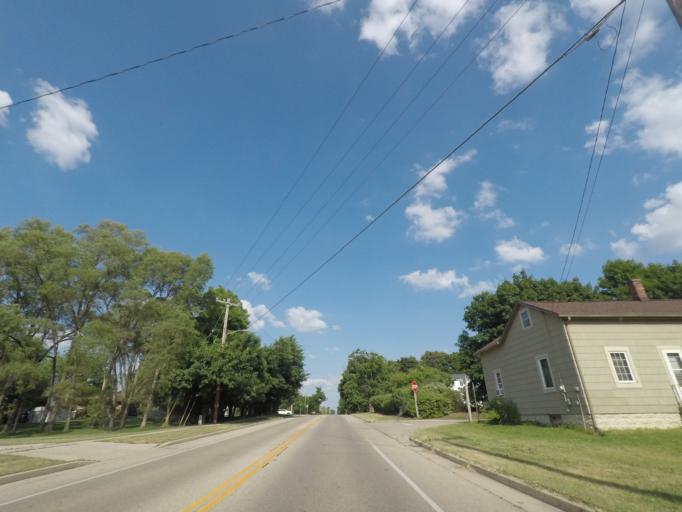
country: US
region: Wisconsin
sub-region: Walworth County
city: East Troy
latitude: 42.7923
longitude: -88.4053
